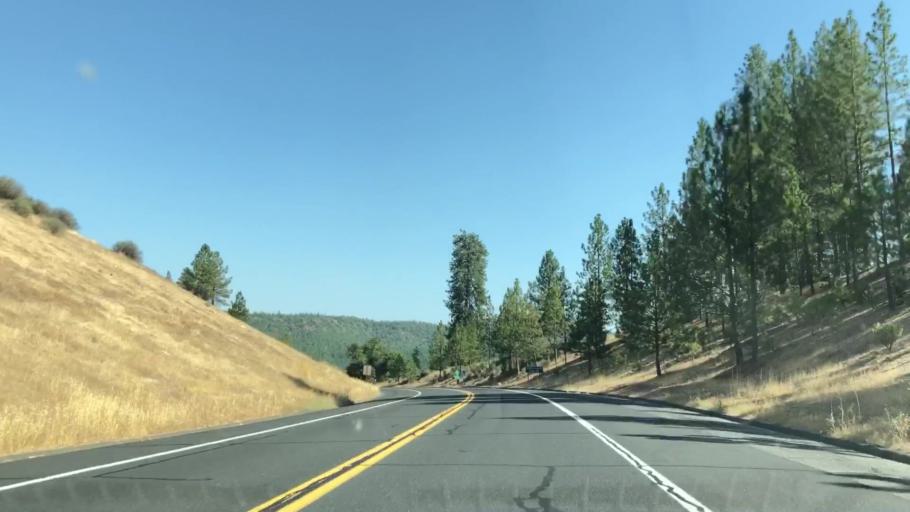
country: US
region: California
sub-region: Tuolumne County
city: Tuolumne City
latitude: 37.8145
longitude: -120.1233
